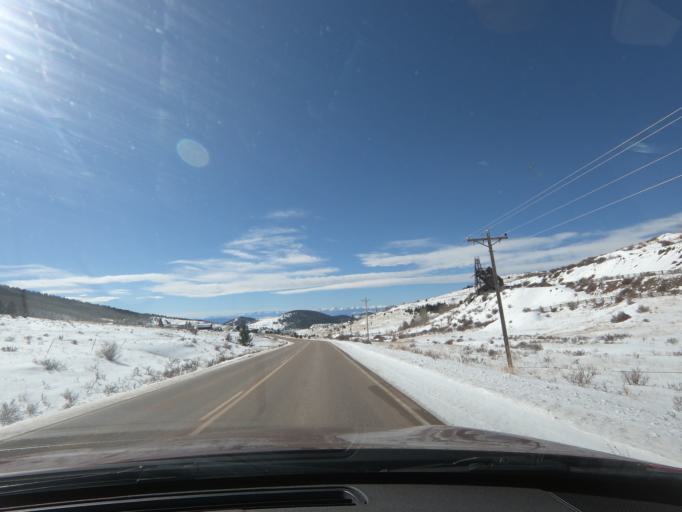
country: US
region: Colorado
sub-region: Teller County
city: Cripple Creek
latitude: 38.7245
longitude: -105.1238
